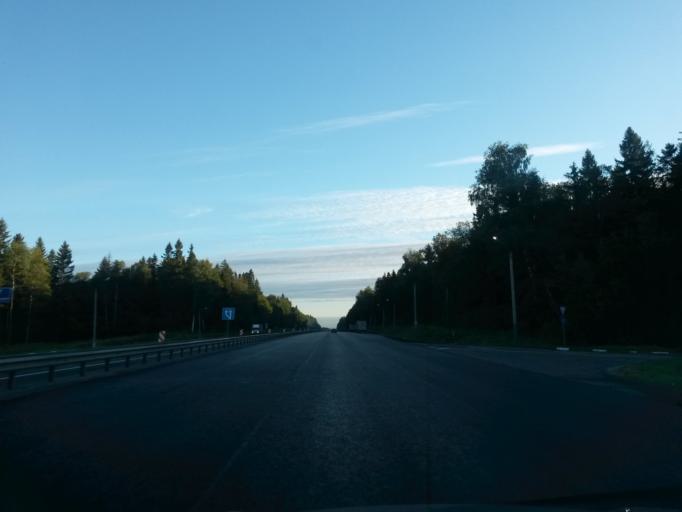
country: RU
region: Moskovskaya
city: Svatkovo
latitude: 56.3919
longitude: 38.3269
